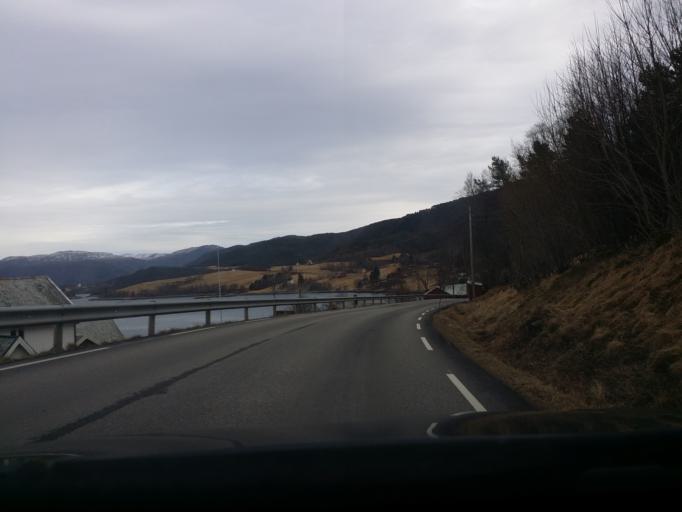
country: NO
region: More og Romsdal
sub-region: Halsa
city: Liaboen
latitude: 63.1394
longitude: 8.4266
